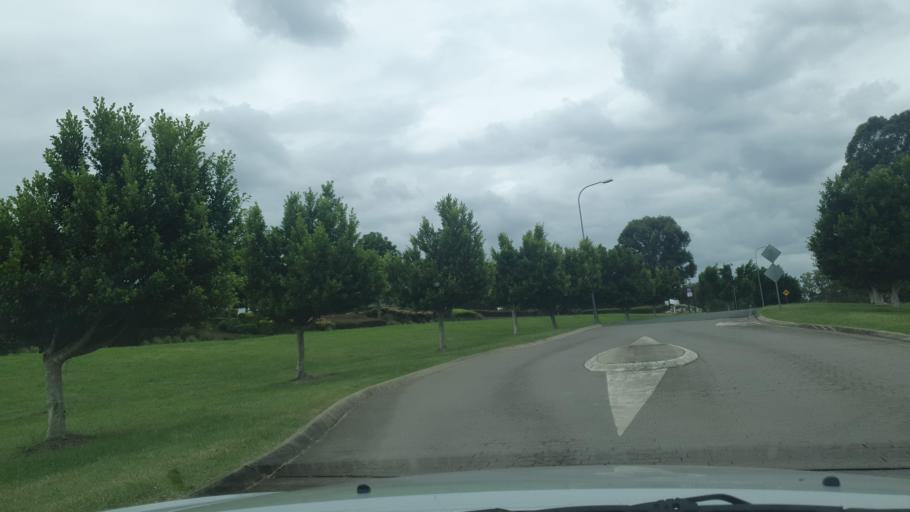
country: AU
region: New South Wales
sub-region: Penrith Municipality
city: Werrington County
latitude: -33.7674
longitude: 150.7439
